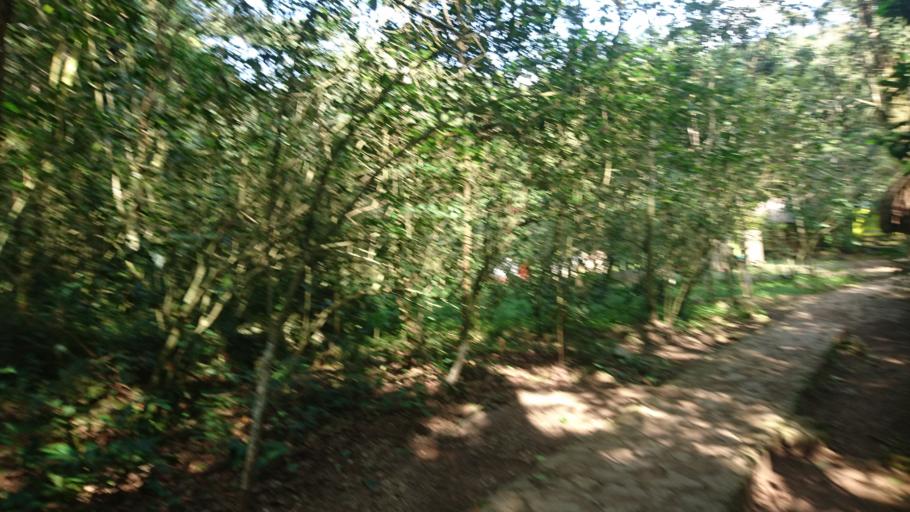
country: MX
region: San Luis Potosi
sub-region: Aquismon
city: Tamapatz
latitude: 21.5249
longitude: -99.0333
